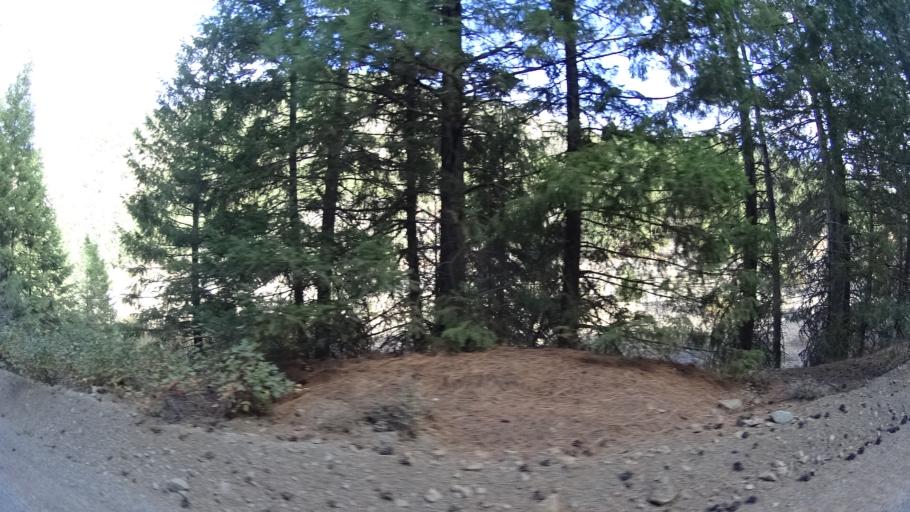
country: US
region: California
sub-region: Siskiyou County
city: Yreka
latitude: 41.7149
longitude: -122.7890
